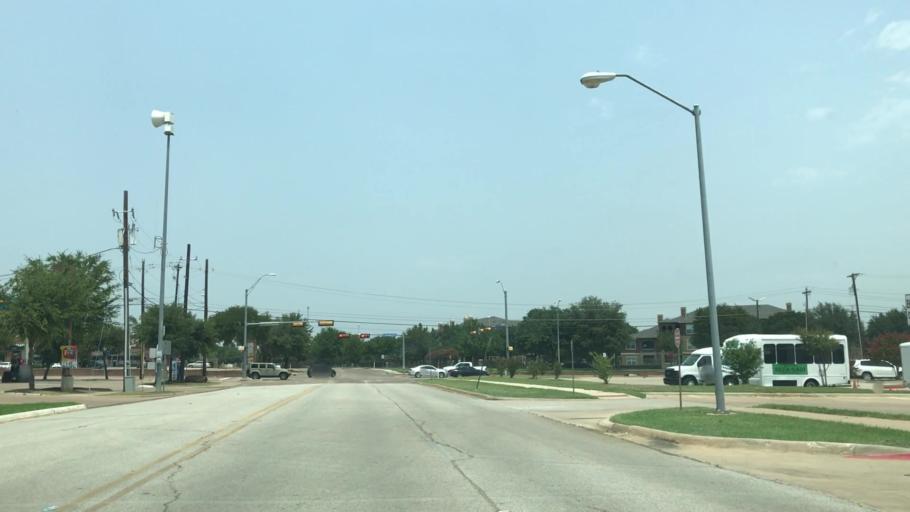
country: US
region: Texas
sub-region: Tarrant County
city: Euless
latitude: 32.8508
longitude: -97.0727
